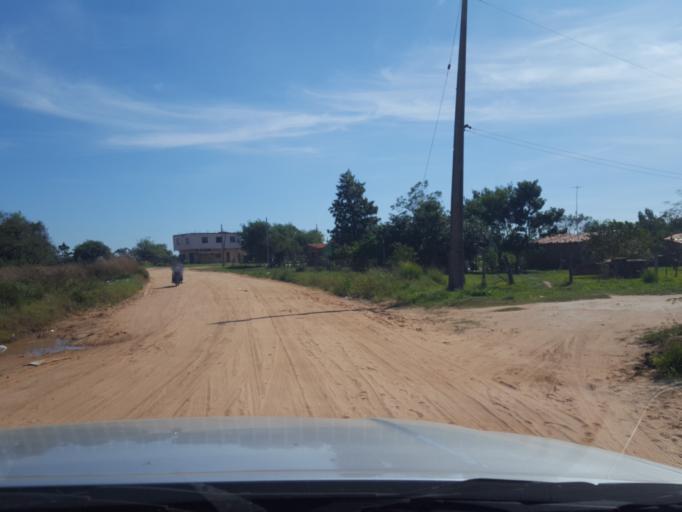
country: PY
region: Cordillera
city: Tobati
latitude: -25.2553
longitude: -57.1005
